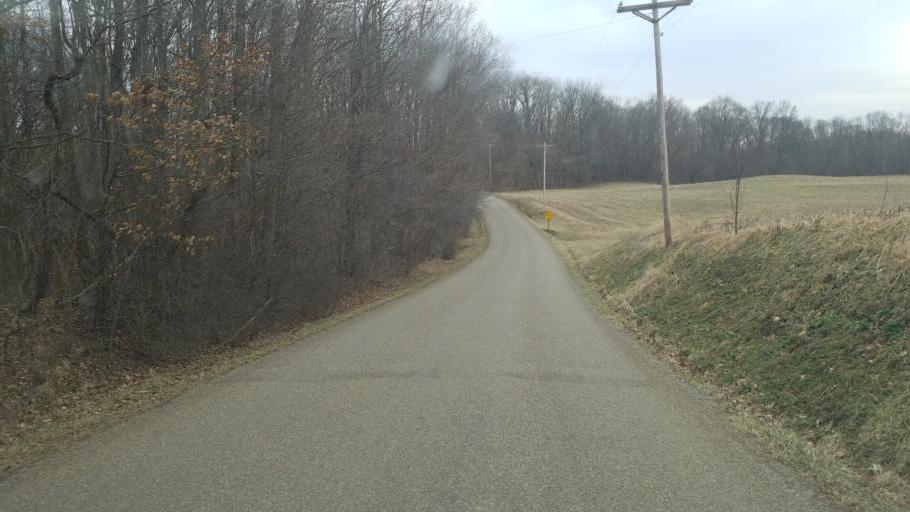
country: US
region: Ohio
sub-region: Richland County
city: Lincoln Heights
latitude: 40.7451
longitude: -82.3792
